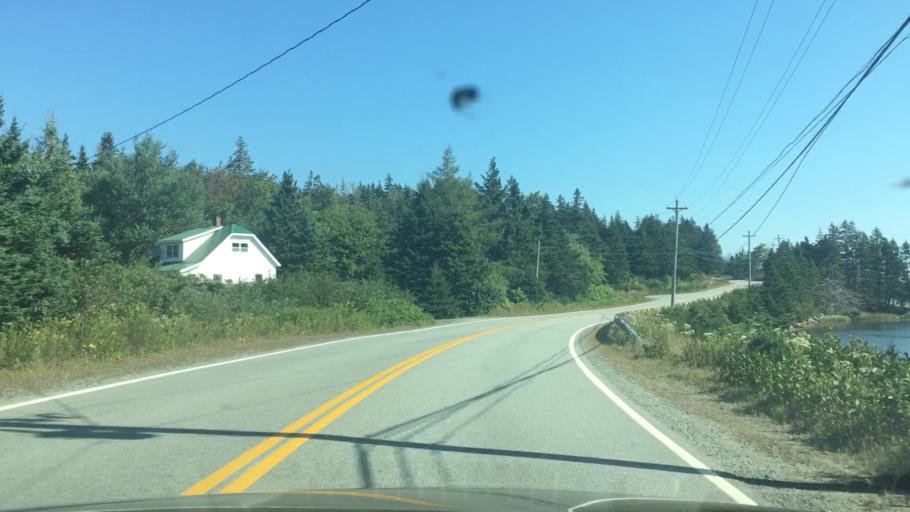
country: CA
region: Nova Scotia
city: New Glasgow
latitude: 44.8226
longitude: -62.6338
